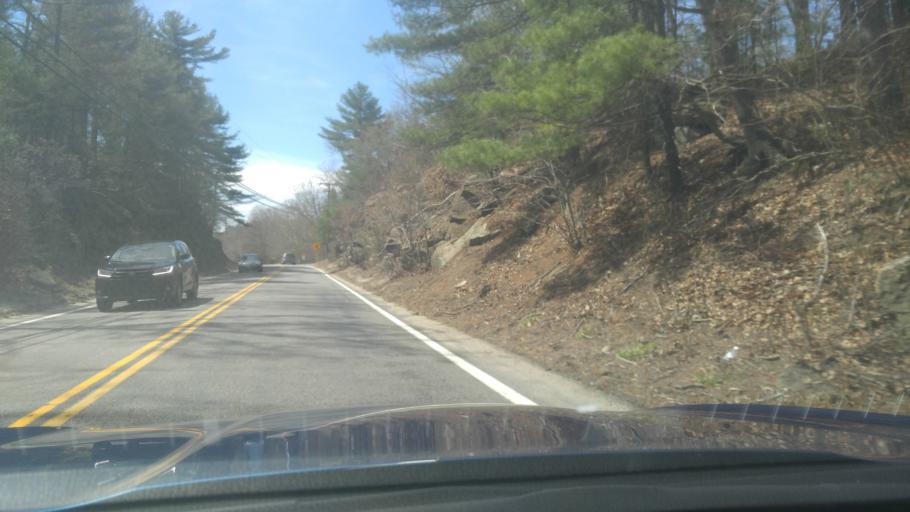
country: US
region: Rhode Island
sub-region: Washington County
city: Exeter
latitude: 41.5795
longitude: -71.5966
